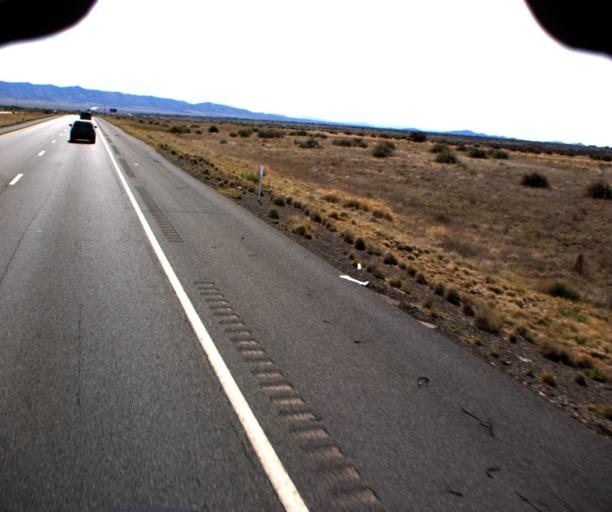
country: US
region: Arizona
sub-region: Yavapai County
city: Prescott Valley
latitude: 34.6305
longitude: -112.3739
